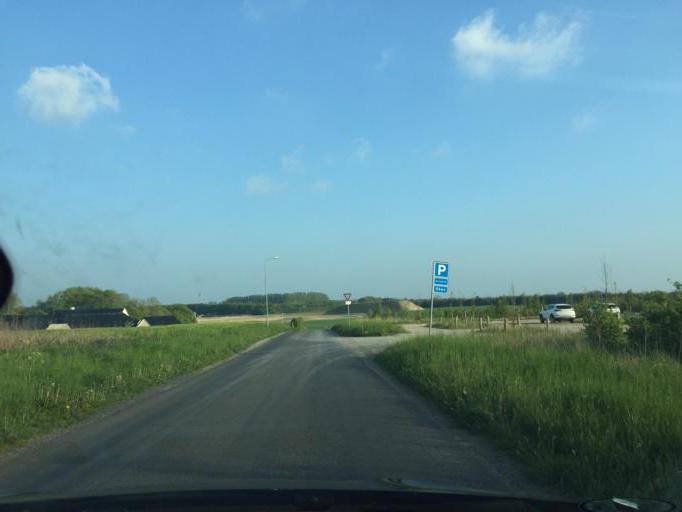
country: DK
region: South Denmark
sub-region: Odense Kommune
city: Bellinge
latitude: 55.3717
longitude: 10.3164
